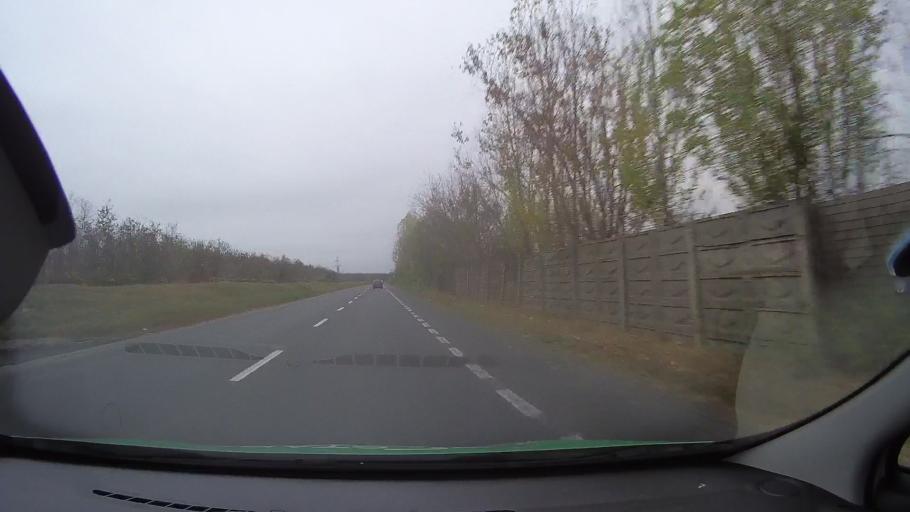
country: RO
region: Ialomita
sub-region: Comuna Slobozia
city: Slobozia
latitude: 44.5580
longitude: 27.3694
